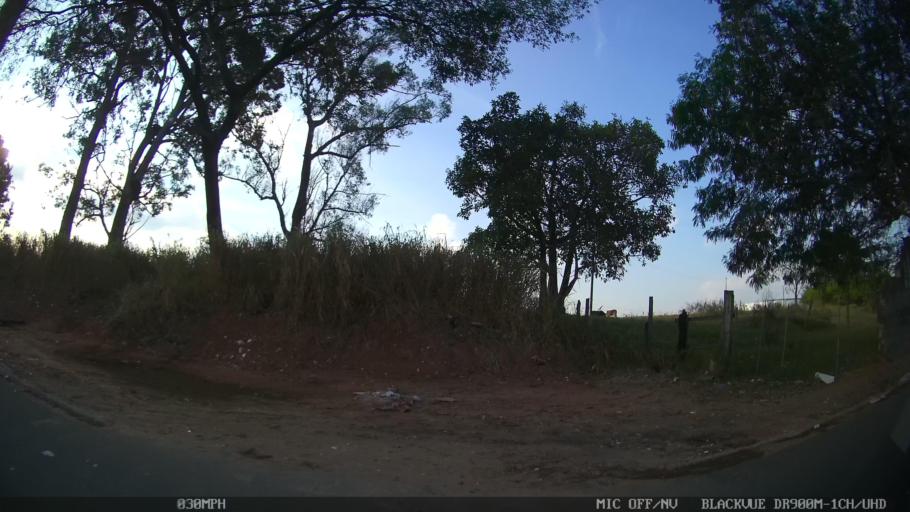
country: BR
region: Sao Paulo
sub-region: Hortolandia
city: Hortolandia
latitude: -22.8768
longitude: -47.1673
